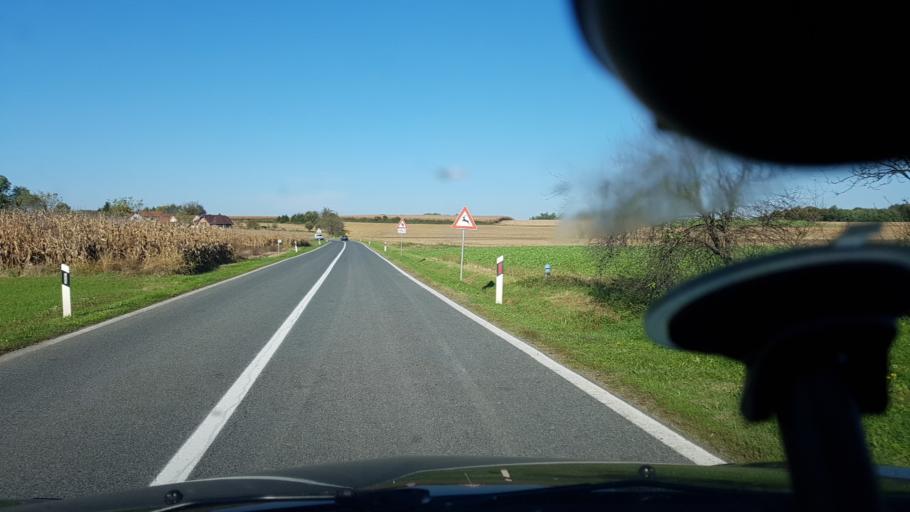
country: HR
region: Bjelovarsko-Bilogorska
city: Gudovac
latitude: 45.8102
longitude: 16.7220
